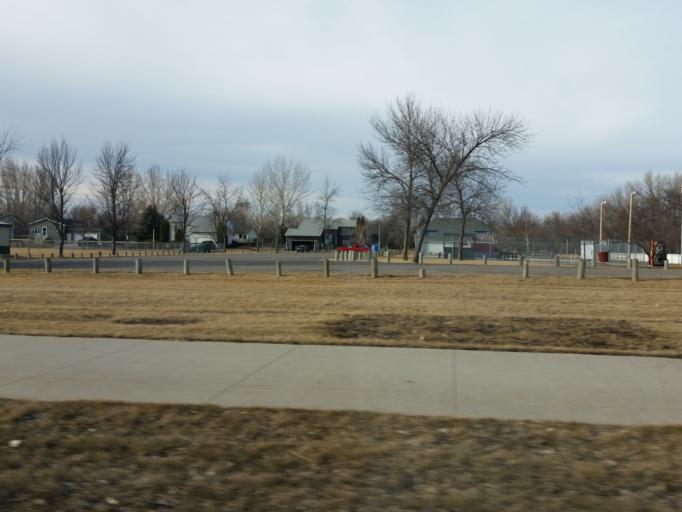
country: US
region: North Dakota
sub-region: Cass County
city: West Fargo
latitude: 46.8626
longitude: -96.9101
